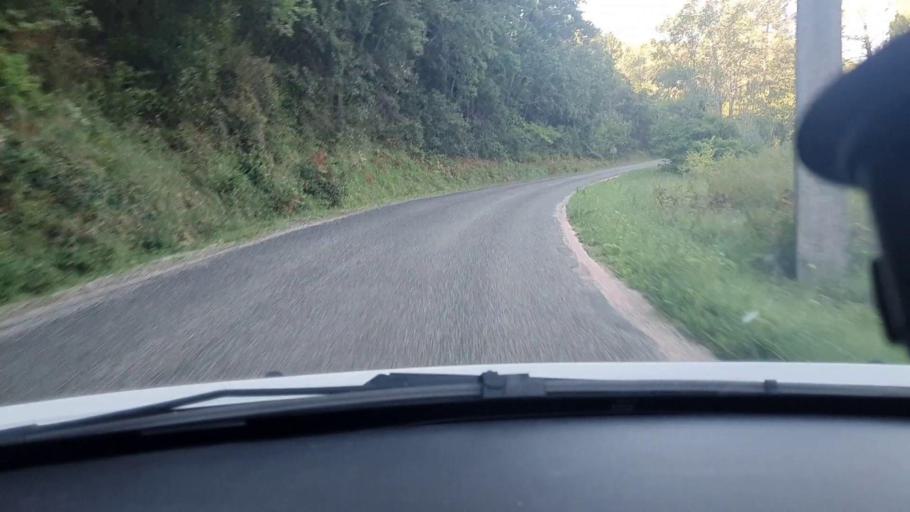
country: FR
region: Languedoc-Roussillon
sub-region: Departement du Gard
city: Goudargues
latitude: 44.1804
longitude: 4.4643
